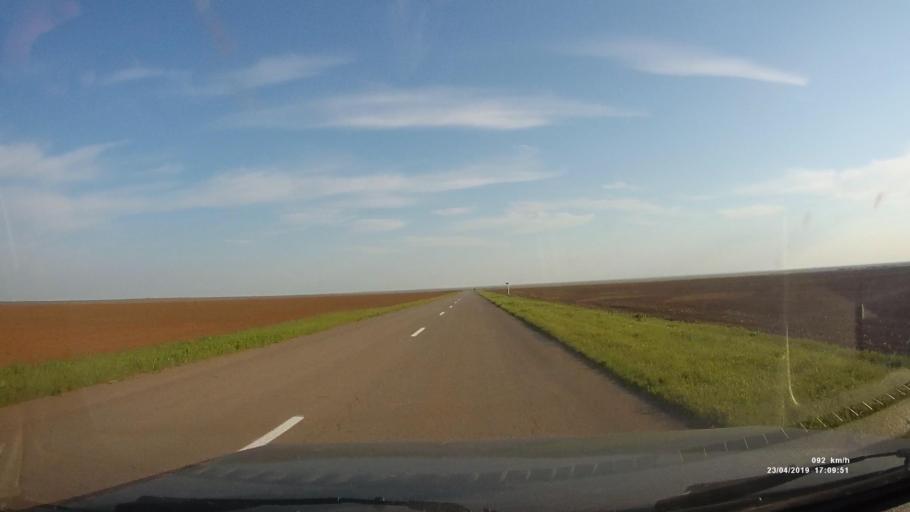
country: RU
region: Kalmykiya
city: Priyutnoye
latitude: 46.2527
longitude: 43.4842
